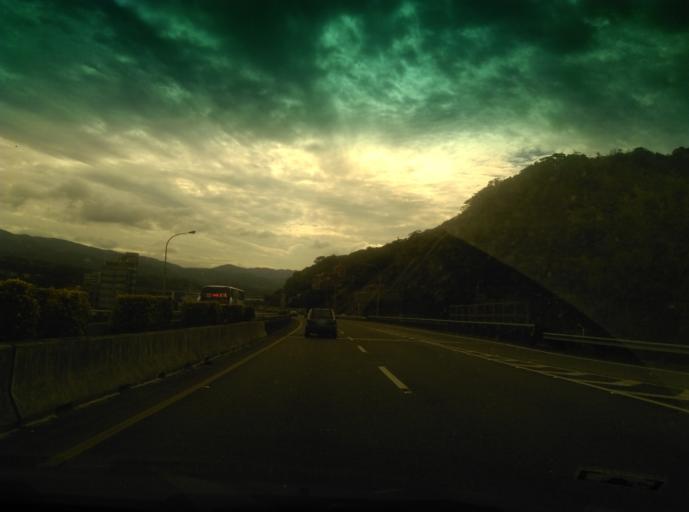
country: TW
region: Taiwan
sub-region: Keelung
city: Keelung
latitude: 25.1155
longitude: 121.7286
